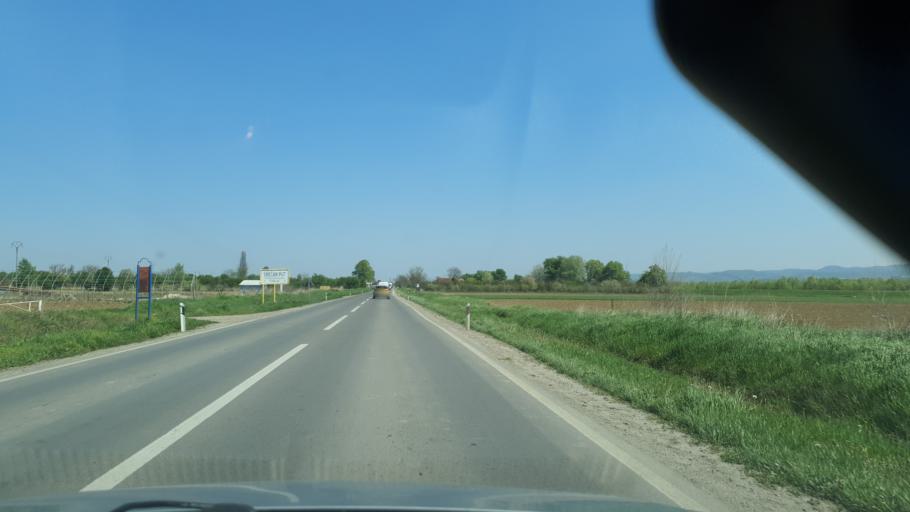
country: RS
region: Autonomna Pokrajina Vojvodina
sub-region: Juznobacki Okrug
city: Beocin
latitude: 45.2419
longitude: 19.6530
